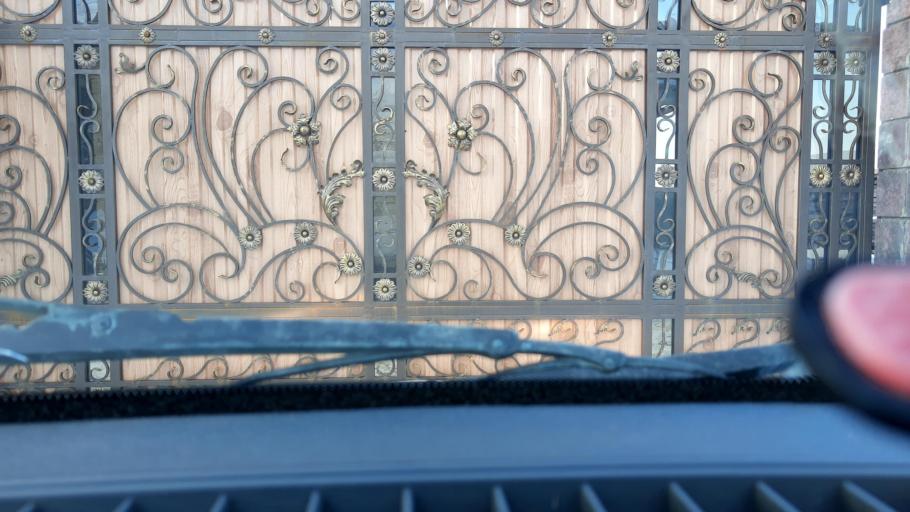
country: RU
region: Bashkortostan
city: Iglino
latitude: 54.7918
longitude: 56.2472
